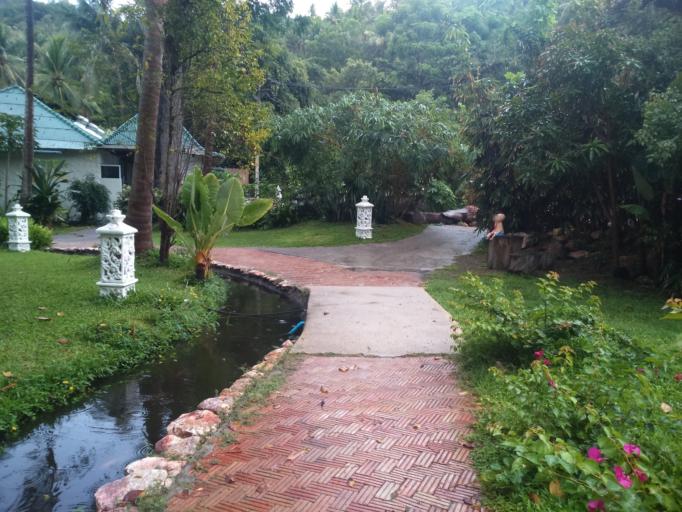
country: TH
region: Surat Thani
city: Ko Samui
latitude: 9.4767
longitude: 100.0673
